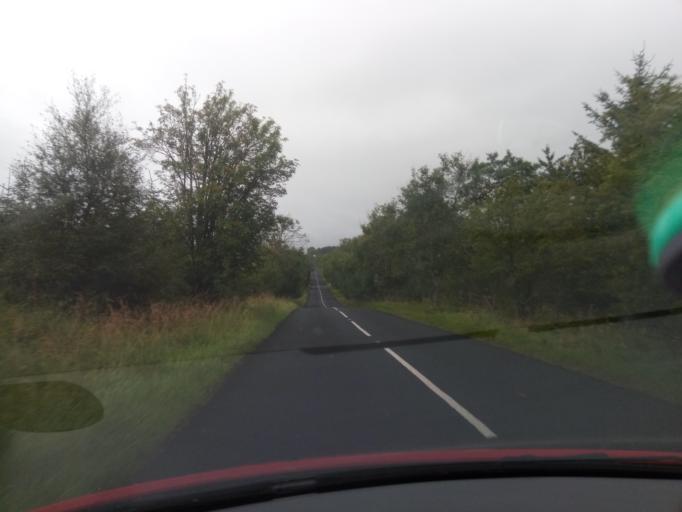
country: GB
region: England
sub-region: Northumberland
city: Rothley
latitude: 55.2008
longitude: -1.9567
